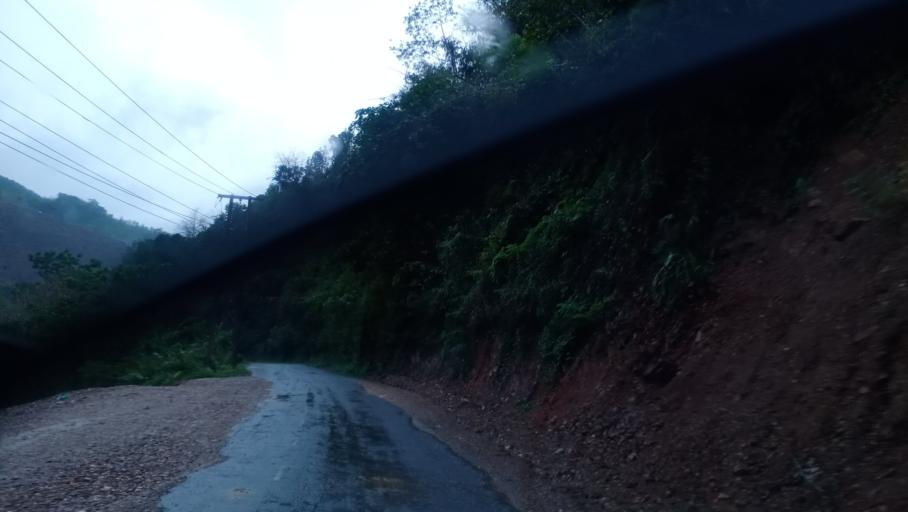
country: LA
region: Phongsali
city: Khoa
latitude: 21.0653
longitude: 102.4856
